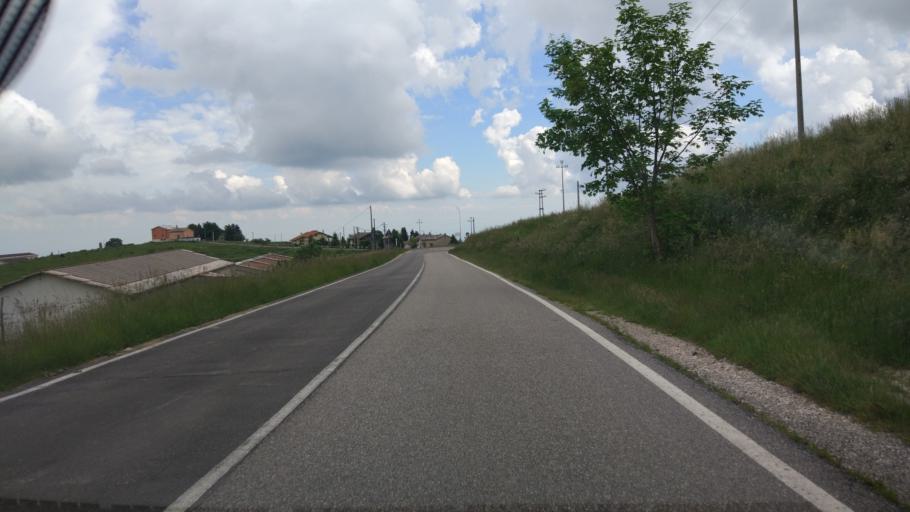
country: IT
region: Veneto
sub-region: Provincia di Verona
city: Bosco Chiesanuova
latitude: 45.6438
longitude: 11.0483
